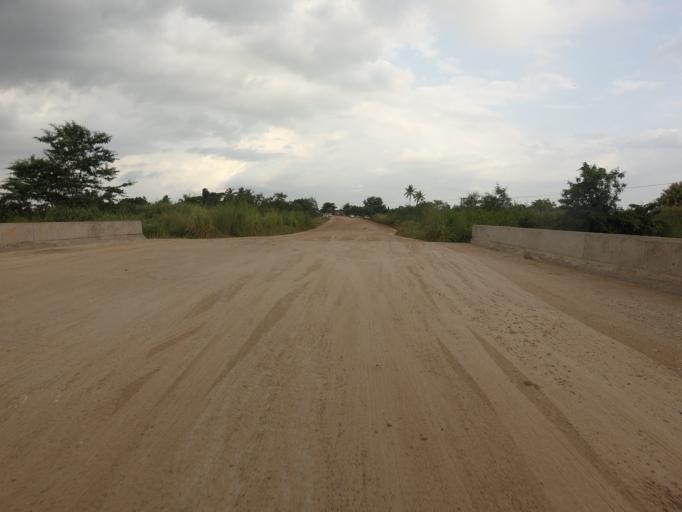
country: GH
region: Volta
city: Ho
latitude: 6.4280
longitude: 0.5098
